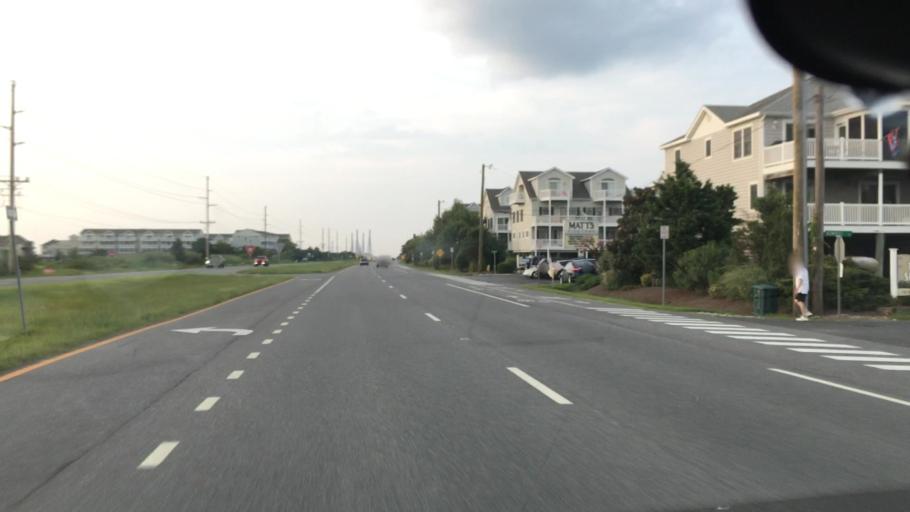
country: US
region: Delaware
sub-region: Sussex County
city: Bethany Beach
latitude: 38.5857
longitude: -75.0617
